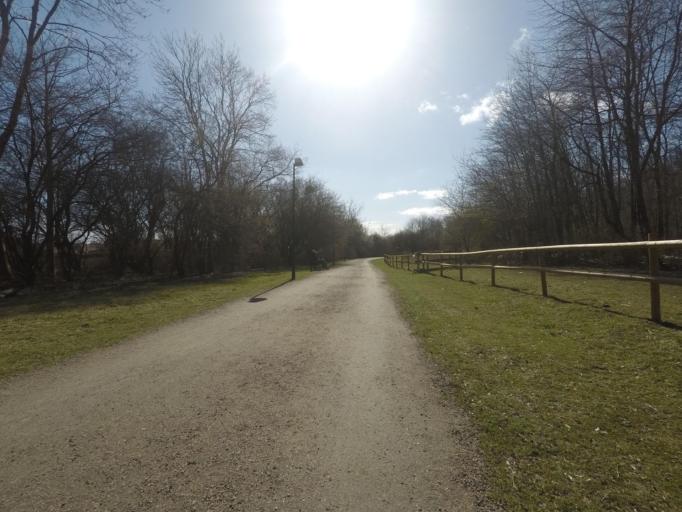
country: SE
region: Skane
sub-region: Burlovs Kommun
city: Arloev
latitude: 55.6046
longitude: 13.0833
